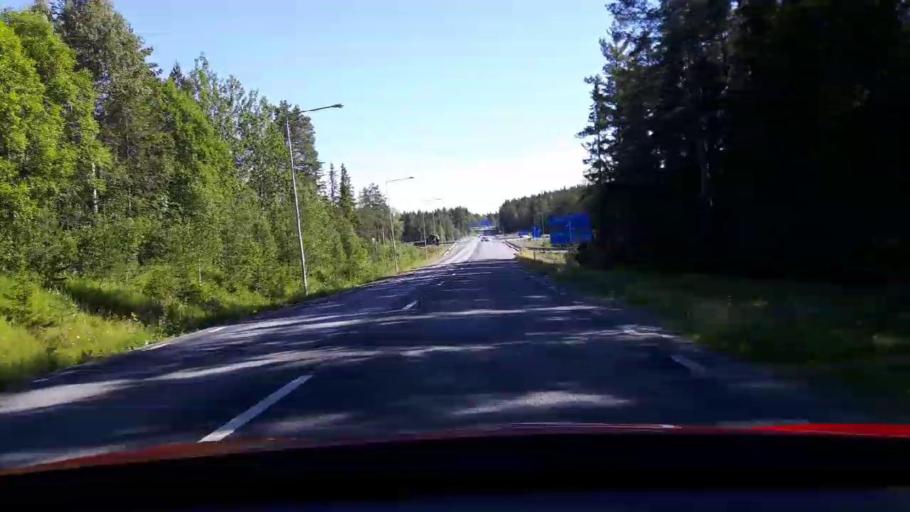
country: SE
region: Jaemtland
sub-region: OEstersunds Kommun
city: Ostersund
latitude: 63.2006
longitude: 14.6738
